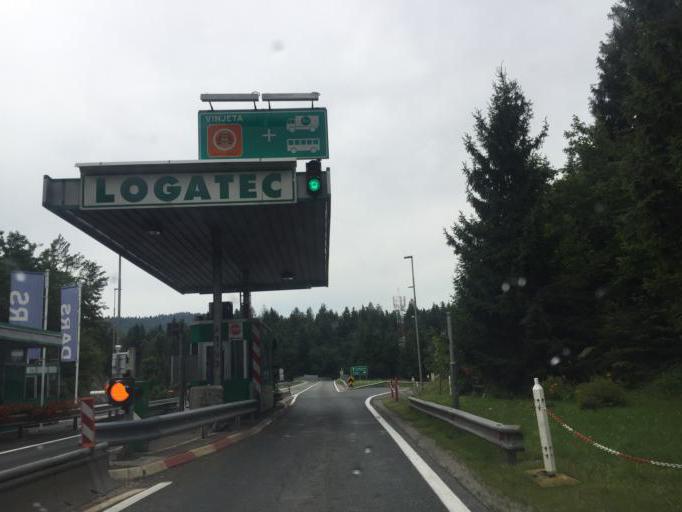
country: SI
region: Logatec
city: Logatec
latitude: 45.9088
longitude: 14.2557
